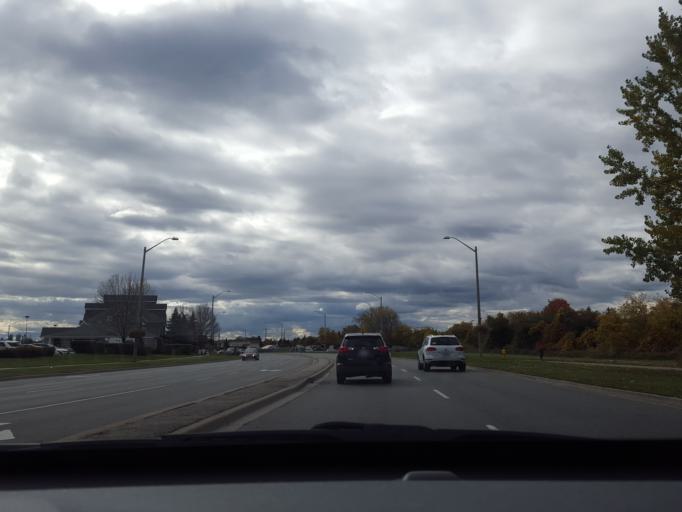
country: CA
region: Ontario
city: Markham
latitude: 43.8275
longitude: -79.3080
